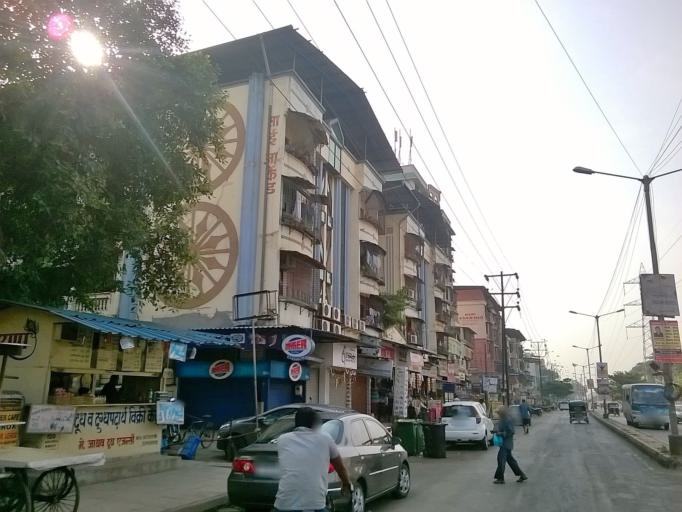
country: IN
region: Maharashtra
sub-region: Raigarh
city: Kalundri
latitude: 18.9912
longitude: 73.1239
